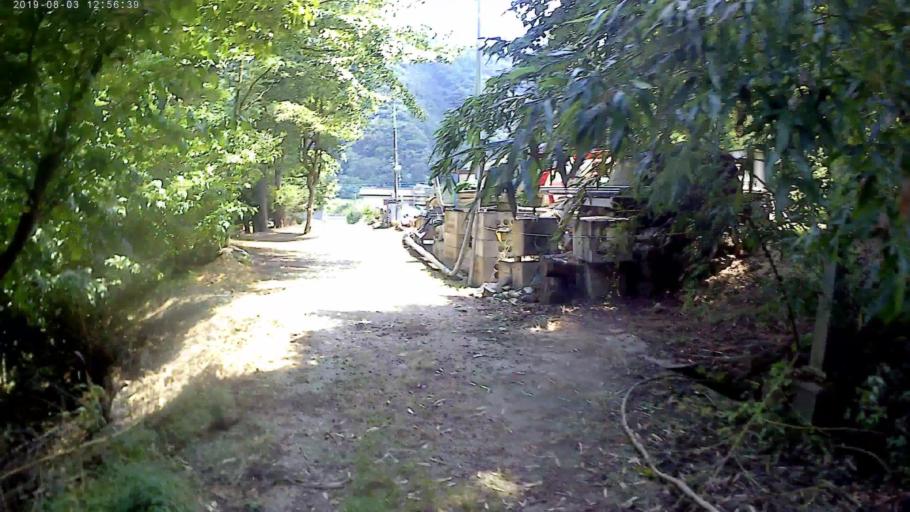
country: JP
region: Yamanashi
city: Enzan
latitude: 35.6030
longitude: 138.8009
